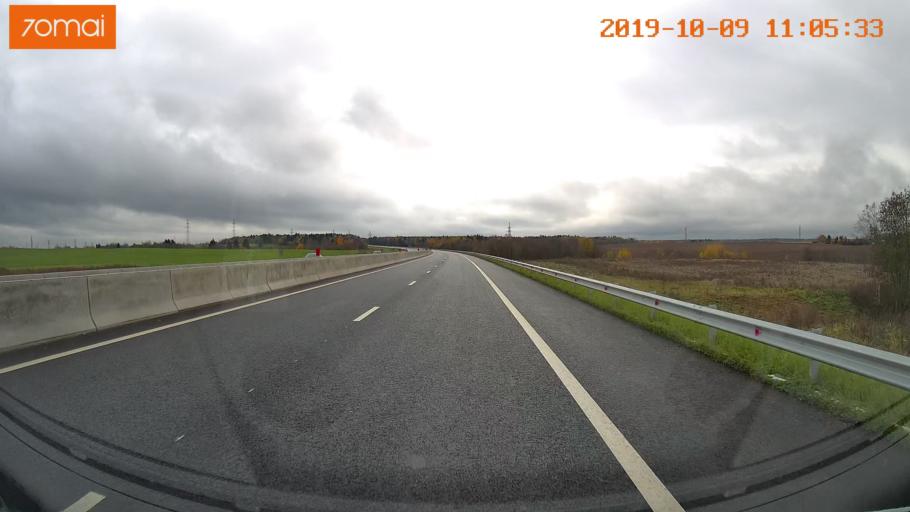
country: RU
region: Vologda
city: Molochnoye
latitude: 59.1986
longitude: 39.7581
